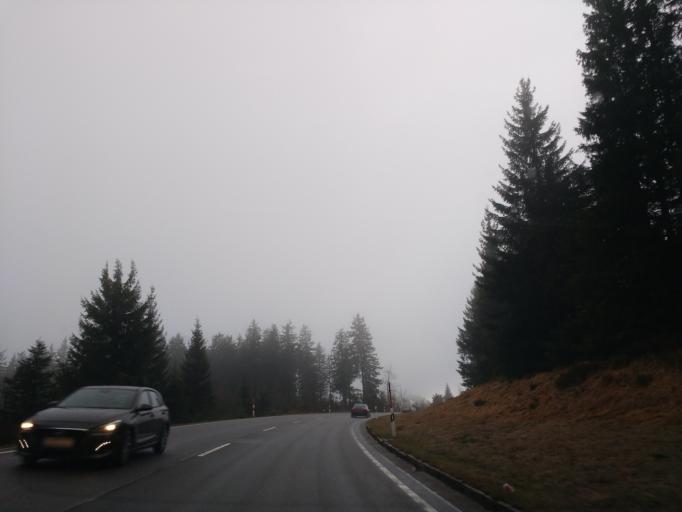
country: DE
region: Baden-Wuerttemberg
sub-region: Freiburg Region
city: Oppenau
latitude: 48.5102
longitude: 8.2242
